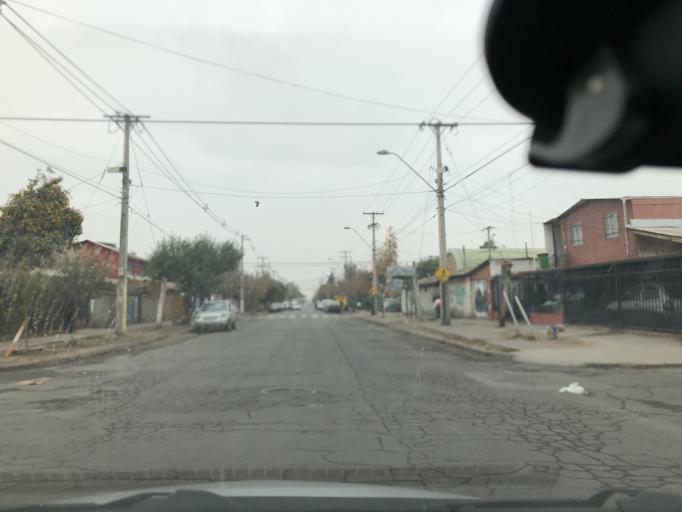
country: CL
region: Santiago Metropolitan
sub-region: Provincia de Santiago
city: La Pintana
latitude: -33.5845
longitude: -70.6031
